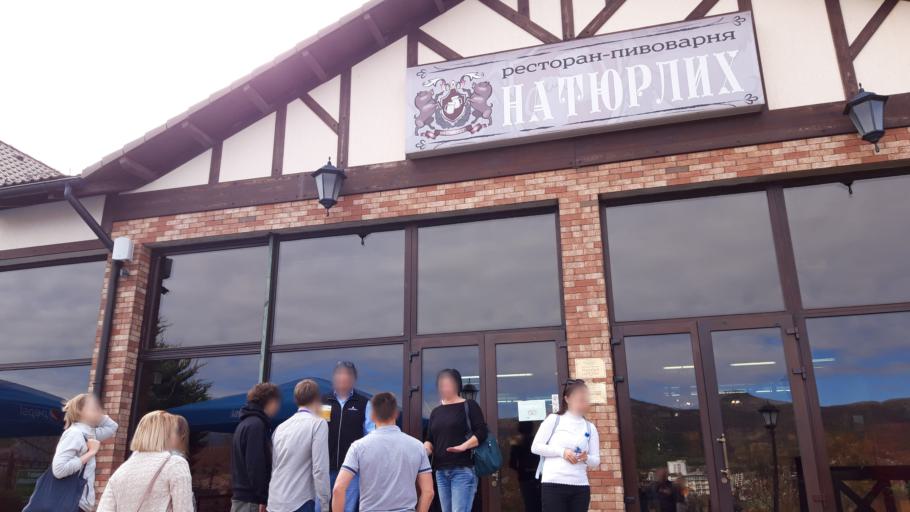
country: RU
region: Krasnodarskiy
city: Kabardinka
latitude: 44.6430
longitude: 37.9356
